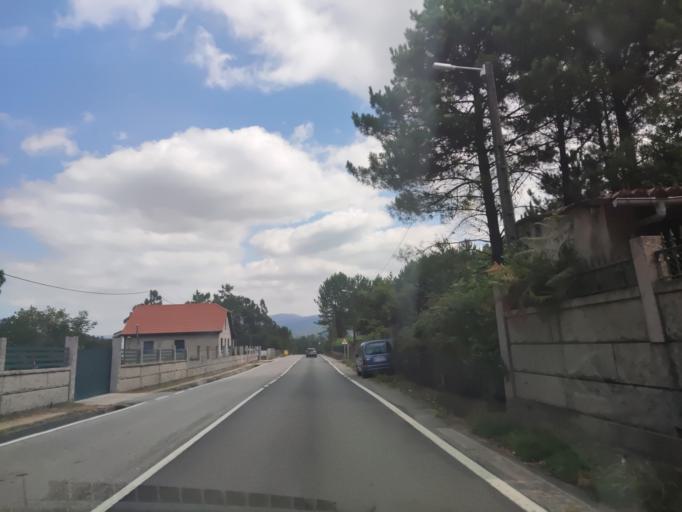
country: ES
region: Galicia
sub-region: Provincia de Pontevedra
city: Porrino
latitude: 42.1467
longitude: -8.6441
